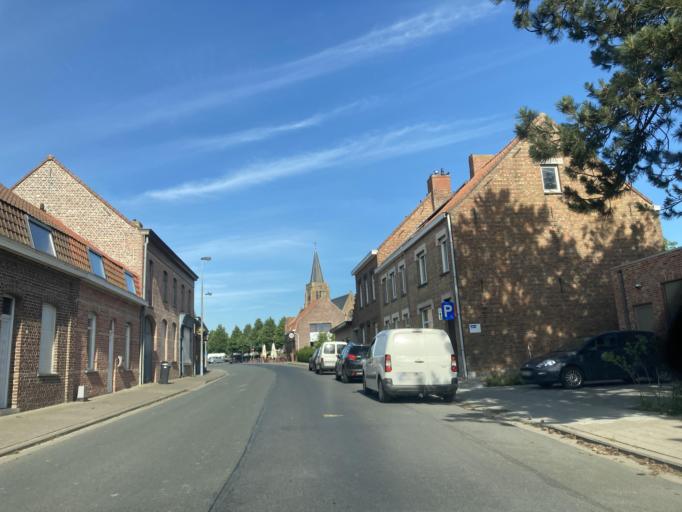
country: FR
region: Nord-Pas-de-Calais
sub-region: Departement du Nord
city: Bailleul
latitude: 50.7660
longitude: 2.7855
